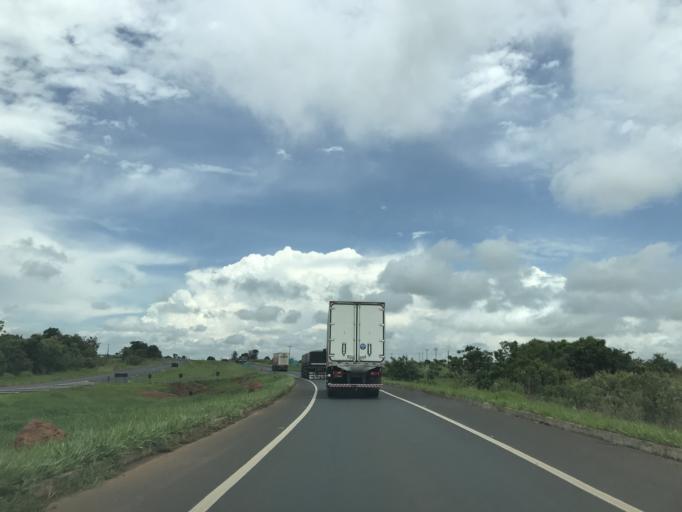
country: BR
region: Minas Gerais
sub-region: Frutal
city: Frutal
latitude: -19.7315
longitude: -48.9730
